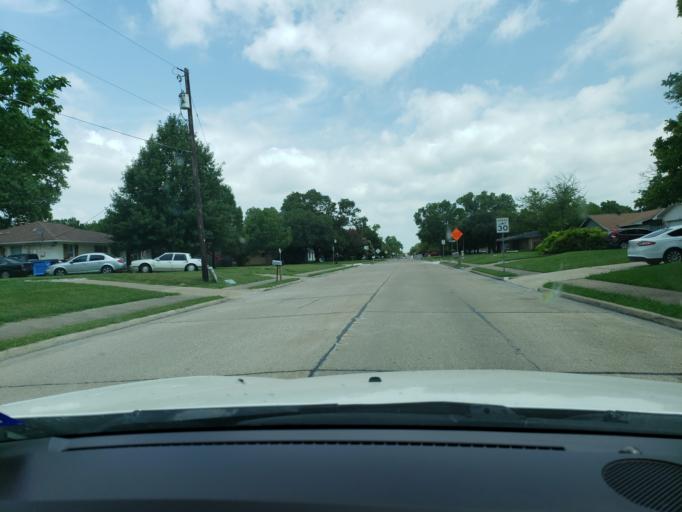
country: US
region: Texas
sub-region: Dallas County
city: Rowlett
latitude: 32.8941
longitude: -96.5630
